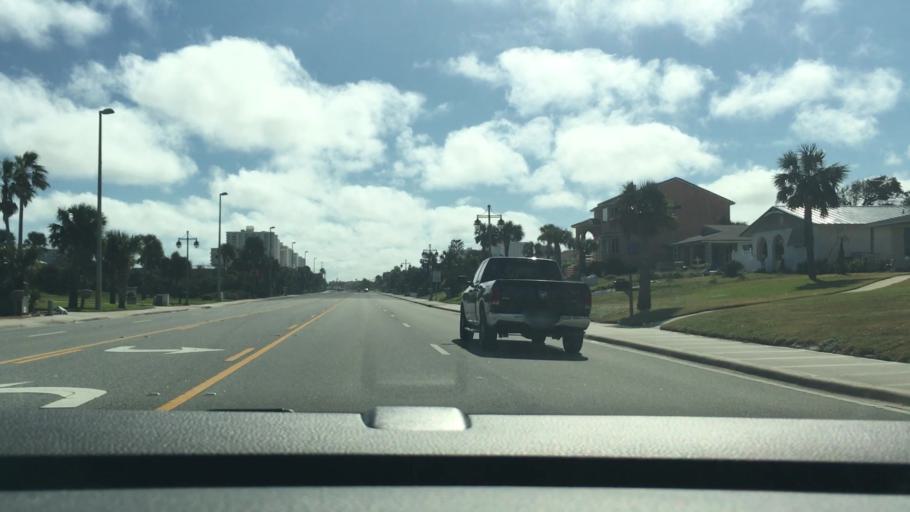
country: US
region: Florida
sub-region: Volusia County
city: Daytona Beach Shores
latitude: 29.1790
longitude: -80.9844
